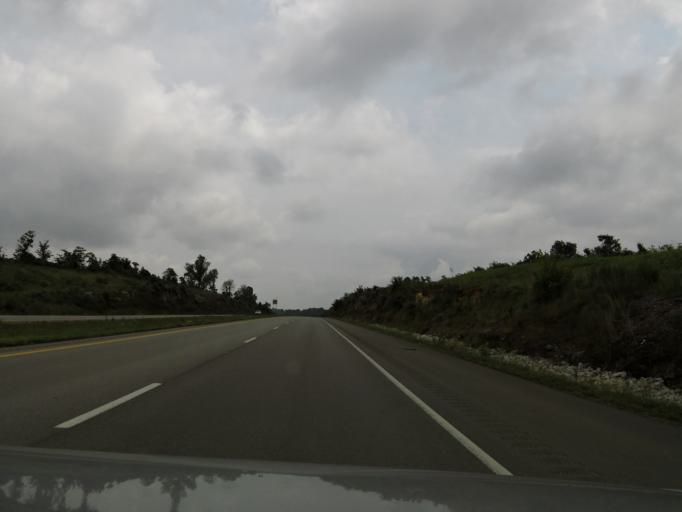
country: US
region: Kentucky
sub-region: Grayson County
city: Leitchfield
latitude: 37.4508
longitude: -86.3331
